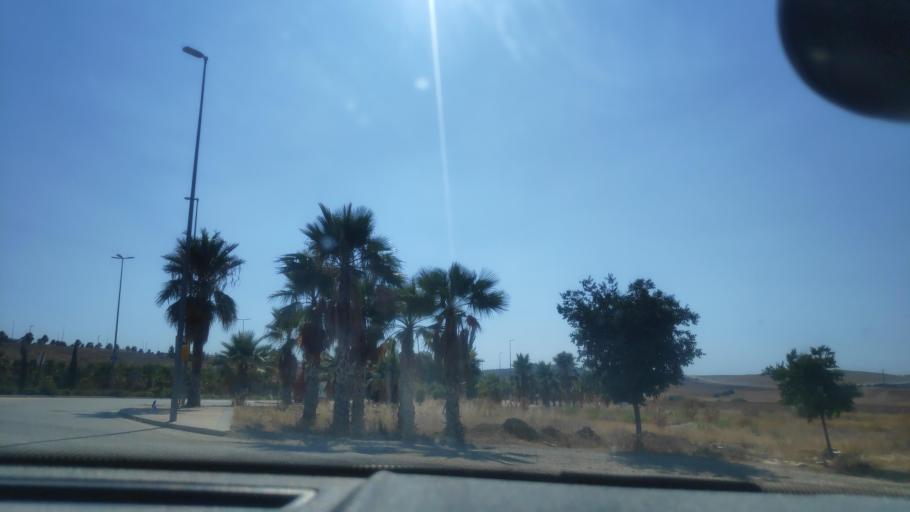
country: ES
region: Andalusia
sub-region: Provincia de Jaen
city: Jaen
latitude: 37.8287
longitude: -3.7694
